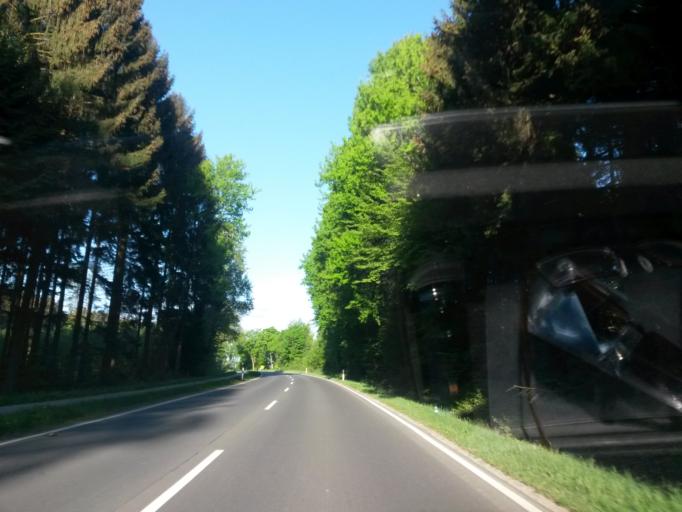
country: DE
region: North Rhine-Westphalia
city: Wiehl
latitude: 50.9288
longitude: 7.5051
